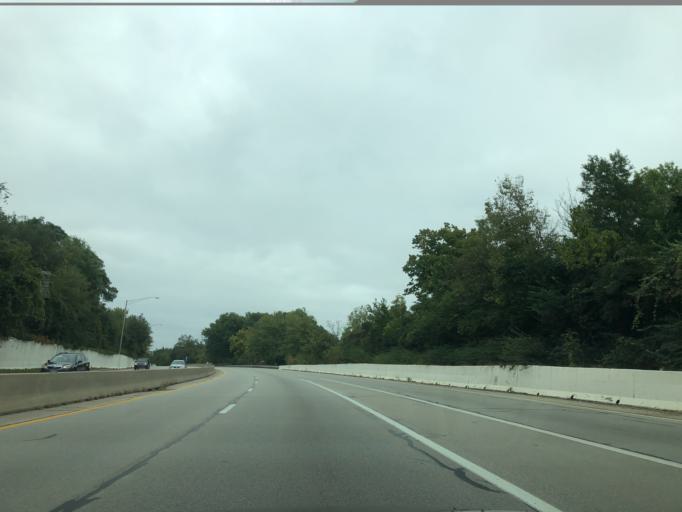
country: US
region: Ohio
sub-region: Hamilton County
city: Amberley
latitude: 39.2166
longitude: -84.4247
